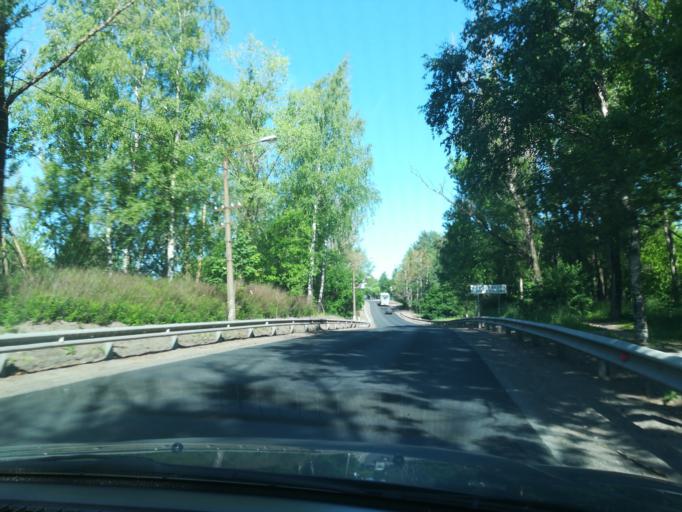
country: RU
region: Leningrad
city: Svetogorsk
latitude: 61.1103
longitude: 28.8585
